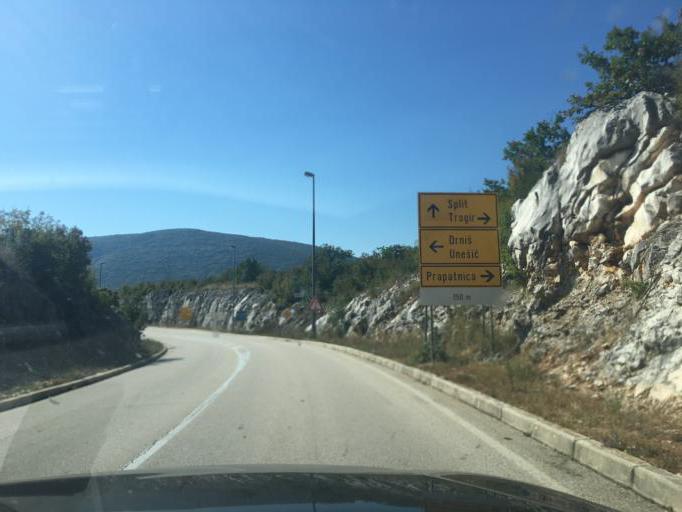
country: HR
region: Splitsko-Dalmatinska
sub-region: Grad Trogir
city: Trogir
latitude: 43.6099
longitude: 16.2232
